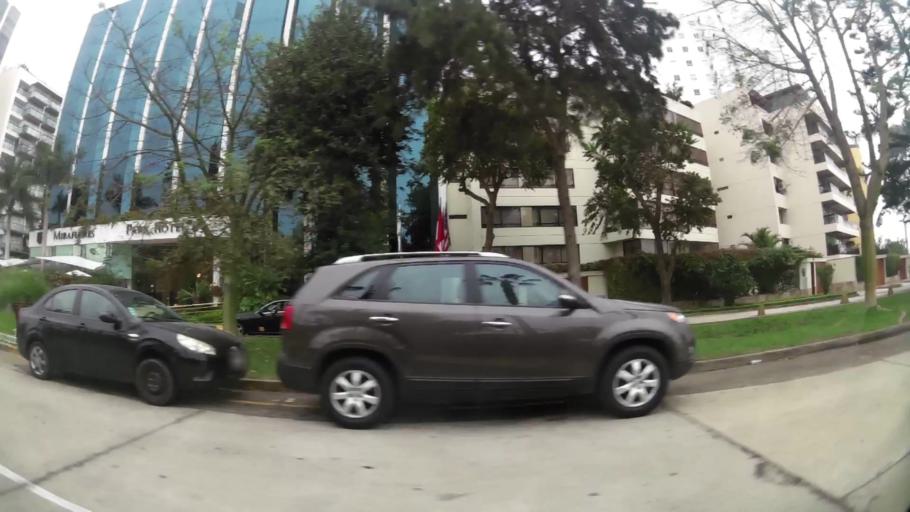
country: PE
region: Lima
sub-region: Lima
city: Surco
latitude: -12.1351
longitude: -77.0277
